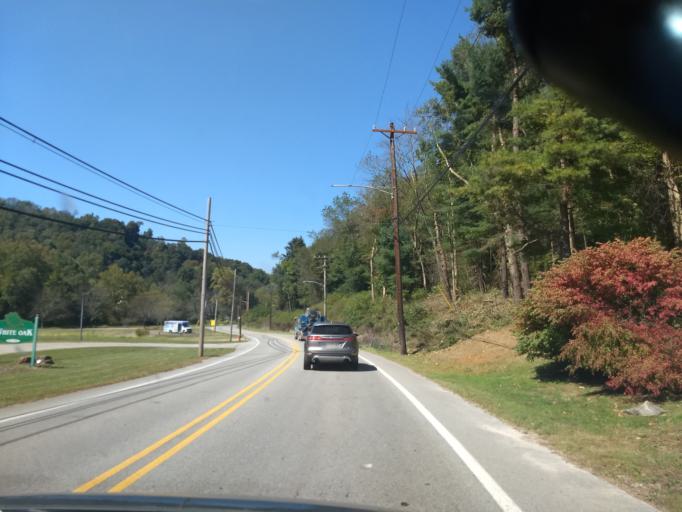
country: US
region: Pennsylvania
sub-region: Allegheny County
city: White Oak
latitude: 40.3309
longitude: -79.7994
